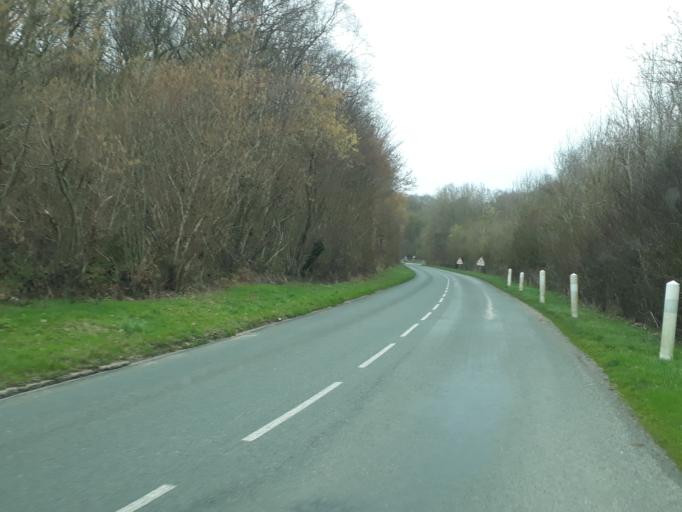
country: FR
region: Haute-Normandie
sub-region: Departement de la Seine-Maritime
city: Les Loges
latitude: 49.6776
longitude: 0.2554
